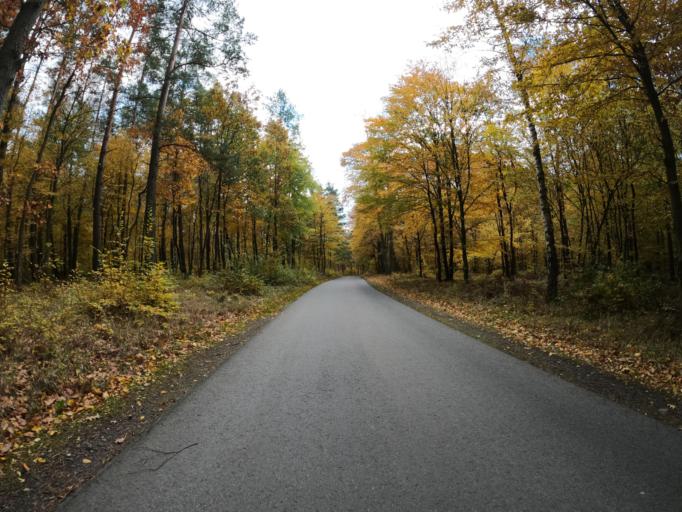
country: PL
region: West Pomeranian Voivodeship
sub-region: Powiat mysliborski
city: Barlinek
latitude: 52.9344
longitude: 15.2854
